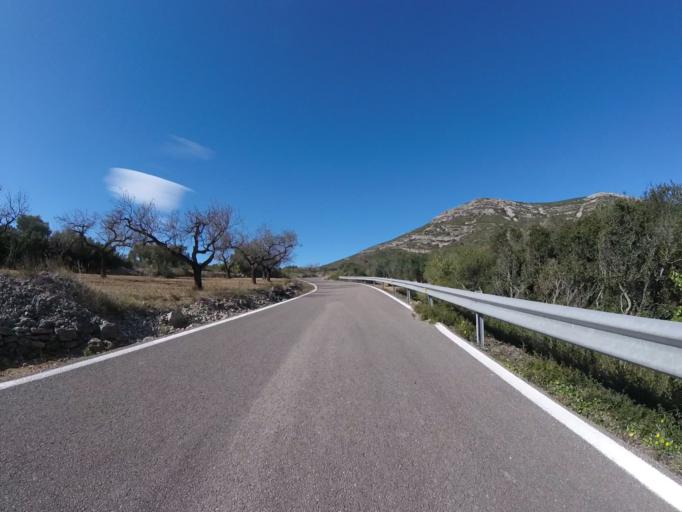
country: ES
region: Valencia
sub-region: Provincia de Castello
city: Albocasser
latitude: 40.3970
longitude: 0.0455
